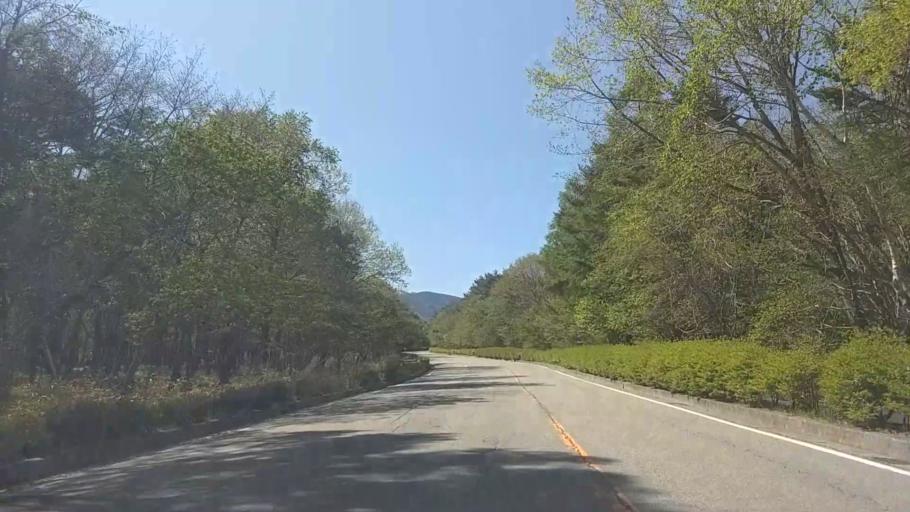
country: JP
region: Yamanashi
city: Nirasaki
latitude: 35.9302
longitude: 138.4282
